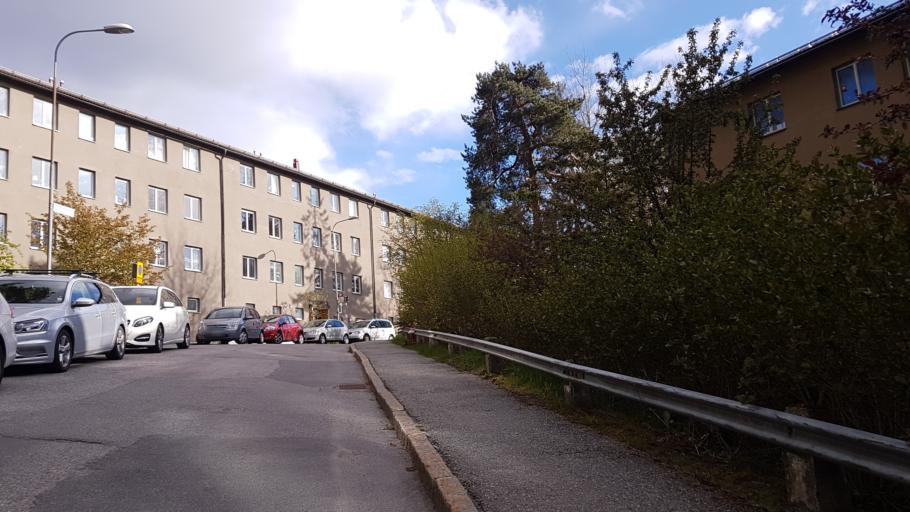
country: SE
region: Stockholm
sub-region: Nacka Kommun
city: Nacka
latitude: 59.2952
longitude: 18.1199
